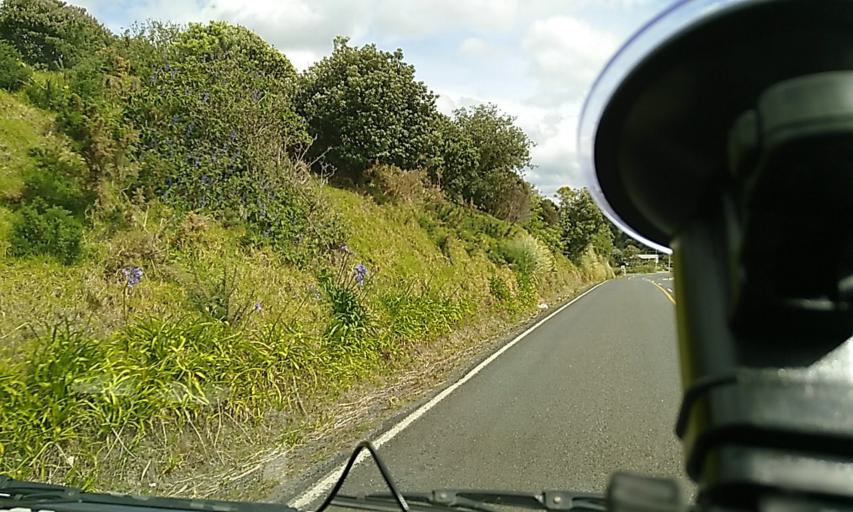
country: NZ
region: Northland
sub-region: Far North District
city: Ahipara
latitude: -35.5144
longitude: 173.3890
